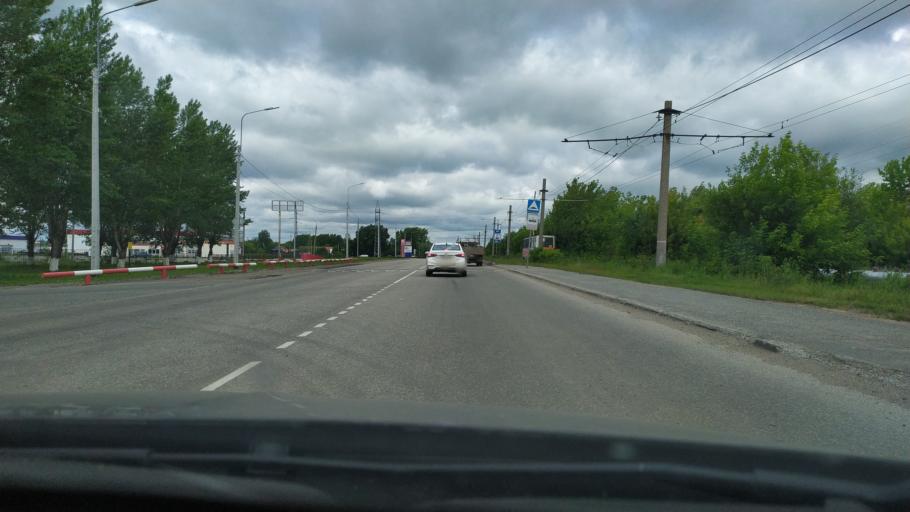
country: RU
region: Perm
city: Kondratovo
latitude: 57.9295
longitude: 56.1303
